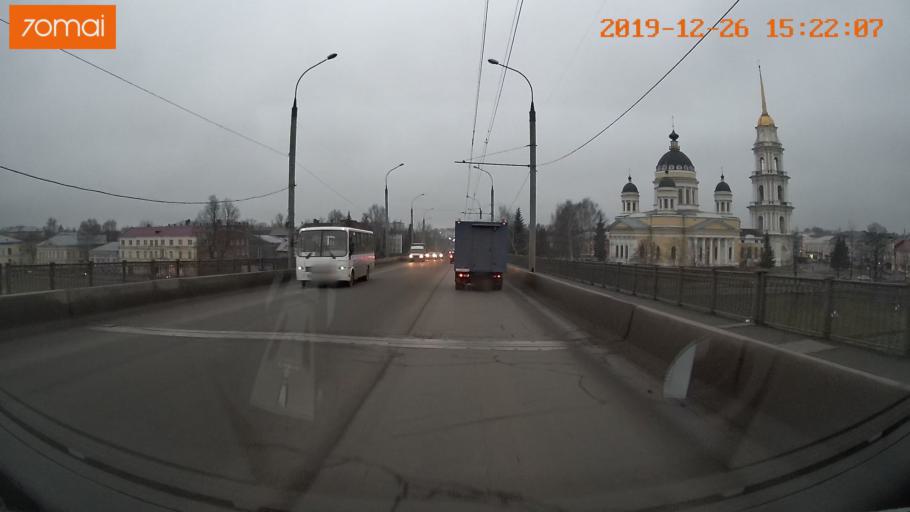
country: RU
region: Jaroslavl
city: Rybinsk
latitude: 58.0494
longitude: 38.8609
